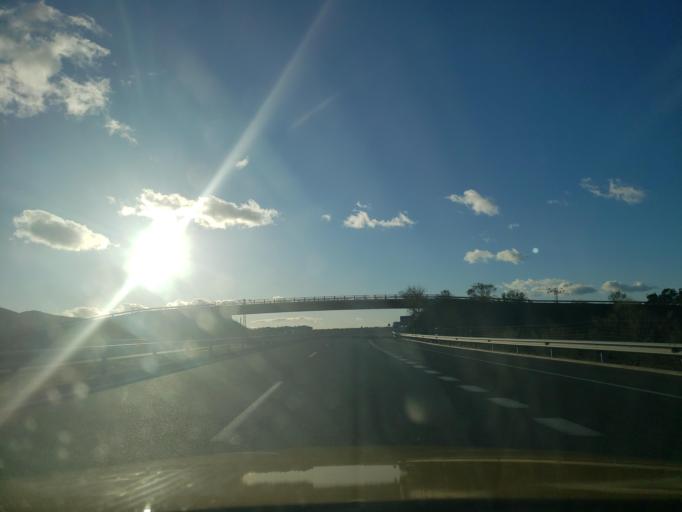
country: ES
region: Castille-La Mancha
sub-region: Province of Toledo
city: Nambroca
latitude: 39.7891
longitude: -3.9414
